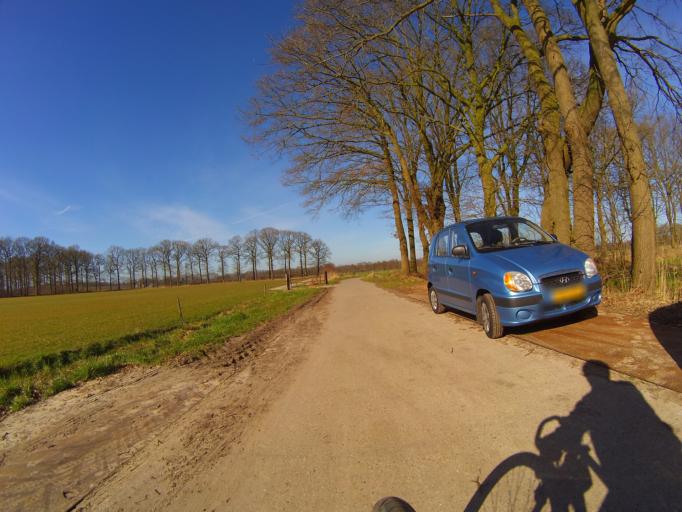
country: NL
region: Utrecht
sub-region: Gemeente Utrechtse Heuvelrug
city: Overberg
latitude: 52.0607
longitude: 5.4910
